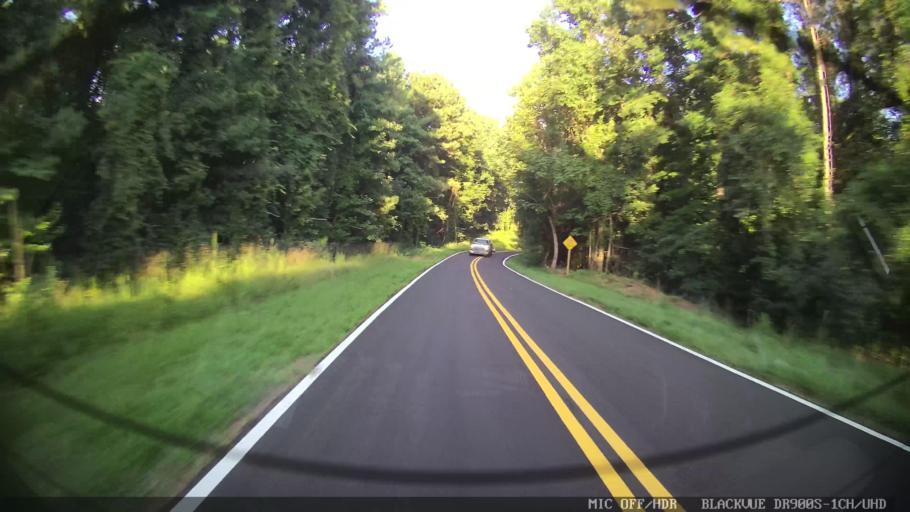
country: US
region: Georgia
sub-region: Bartow County
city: Emerson
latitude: 34.2034
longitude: -84.6823
